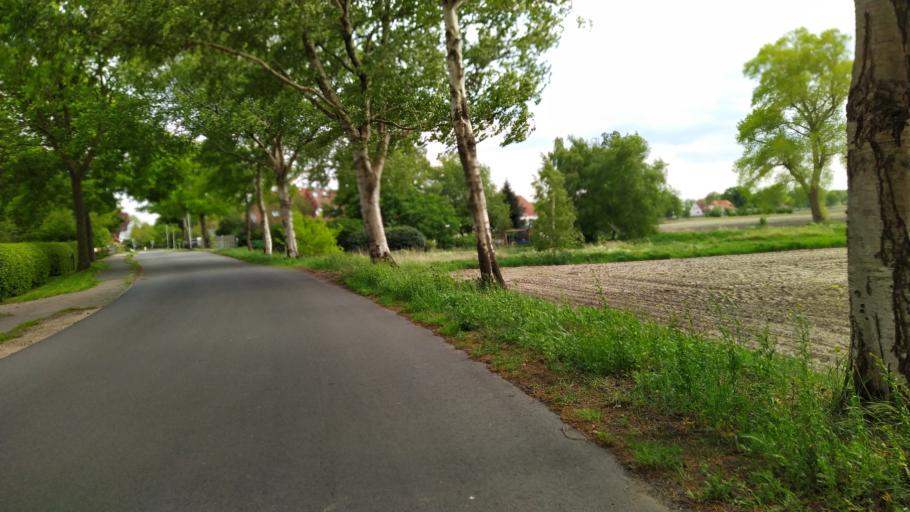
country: DE
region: Lower Saxony
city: Grasberg
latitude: 53.1936
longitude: 9.0181
